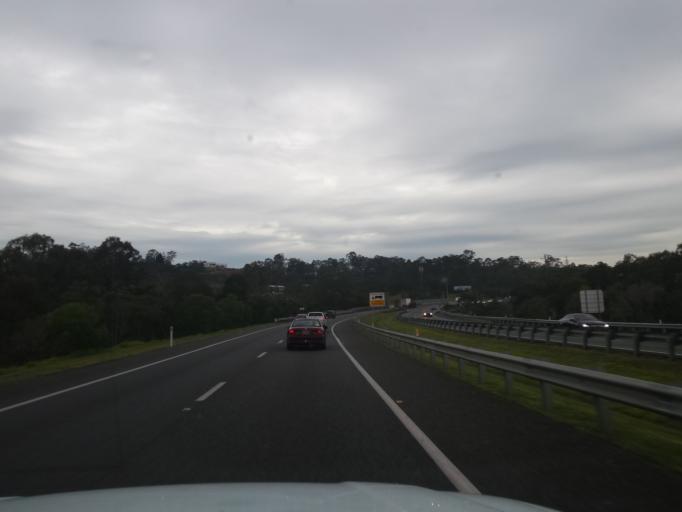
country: AU
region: Queensland
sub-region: Logan
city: Slacks Creek
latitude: -27.6666
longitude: 153.1583
